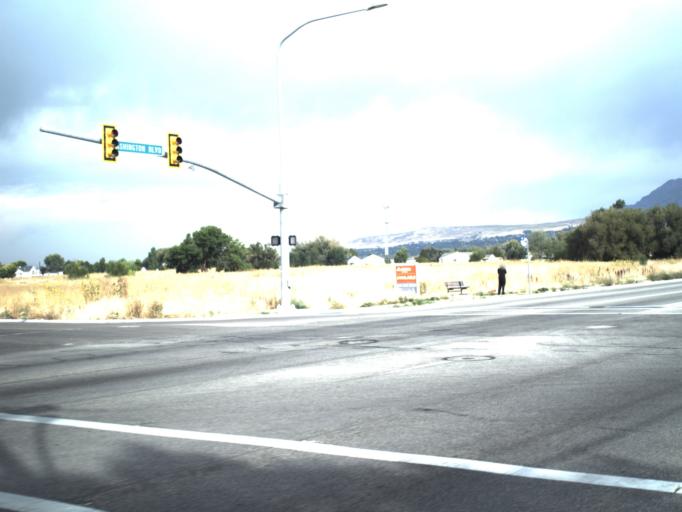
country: US
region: Utah
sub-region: Weber County
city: North Ogden
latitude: 41.2887
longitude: -111.9690
